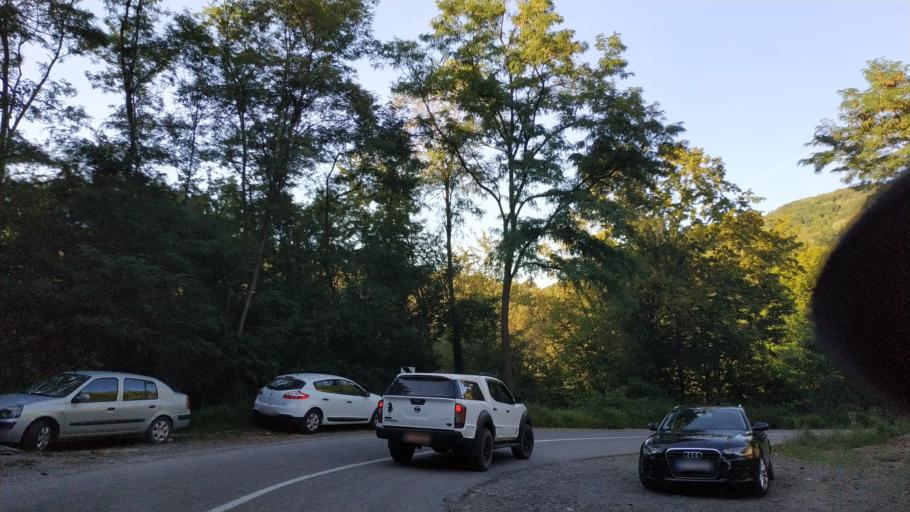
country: RS
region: Central Serbia
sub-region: Rasinski Okrug
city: Krusevac
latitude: 43.4584
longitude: 21.3589
